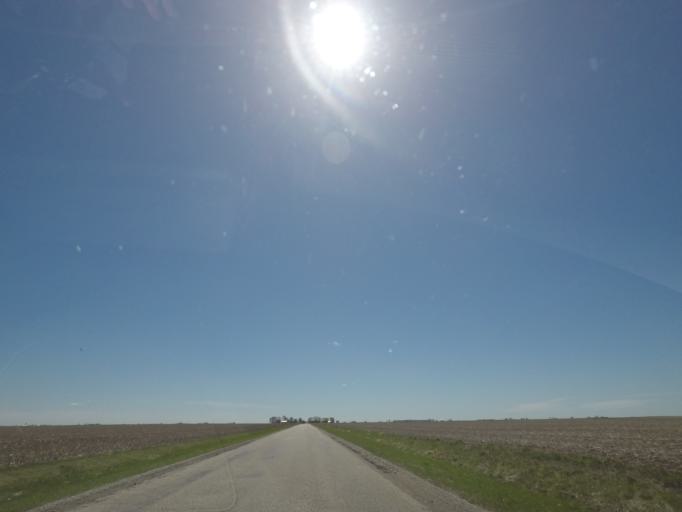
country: US
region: Illinois
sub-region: Logan County
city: Atlanta
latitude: 40.1929
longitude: -89.1941
